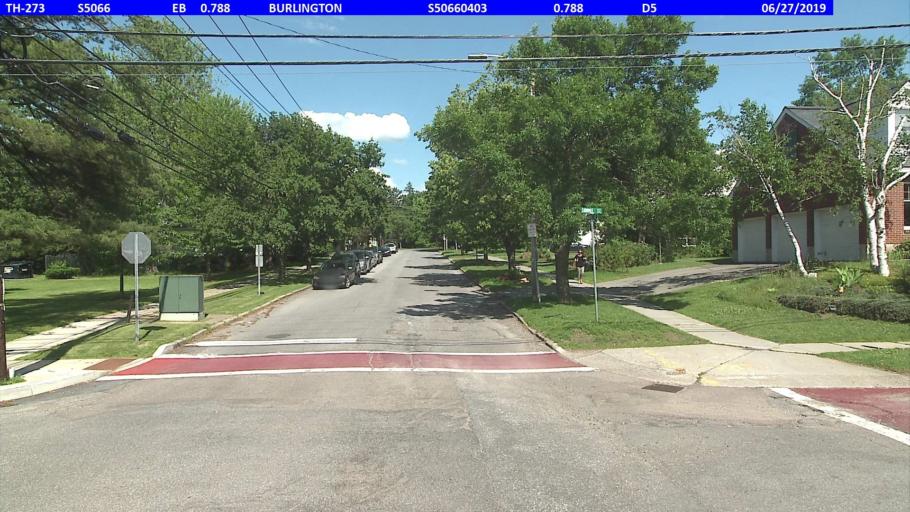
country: US
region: Vermont
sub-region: Chittenden County
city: Burlington
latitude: 44.4740
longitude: -73.2023
